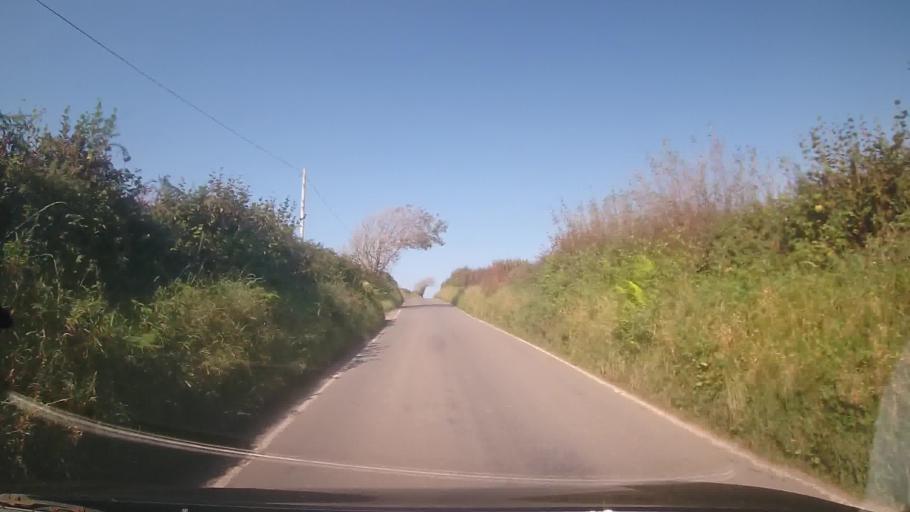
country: GB
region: Wales
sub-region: Pembrokeshire
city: Camrose
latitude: 51.8584
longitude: -5.0141
